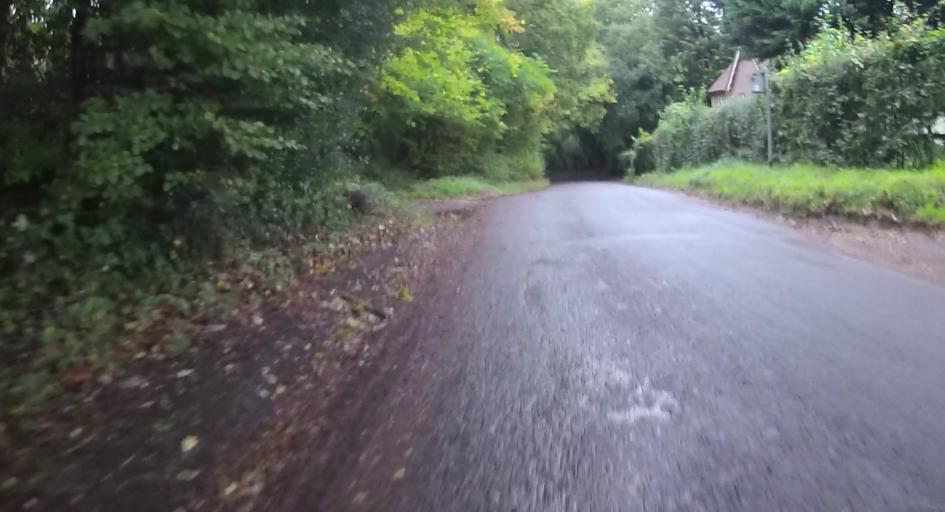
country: GB
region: England
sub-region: West Berkshire
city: Thatcham
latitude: 51.4161
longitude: -1.1799
